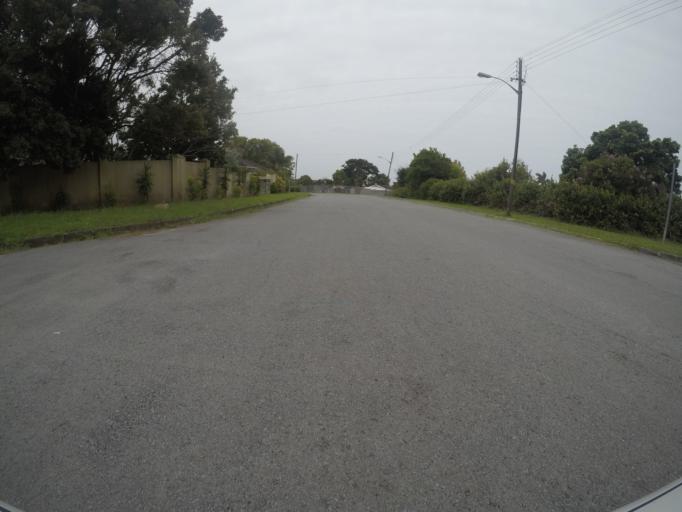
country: ZA
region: Eastern Cape
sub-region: Buffalo City Metropolitan Municipality
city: East London
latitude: -32.9711
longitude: 27.9378
